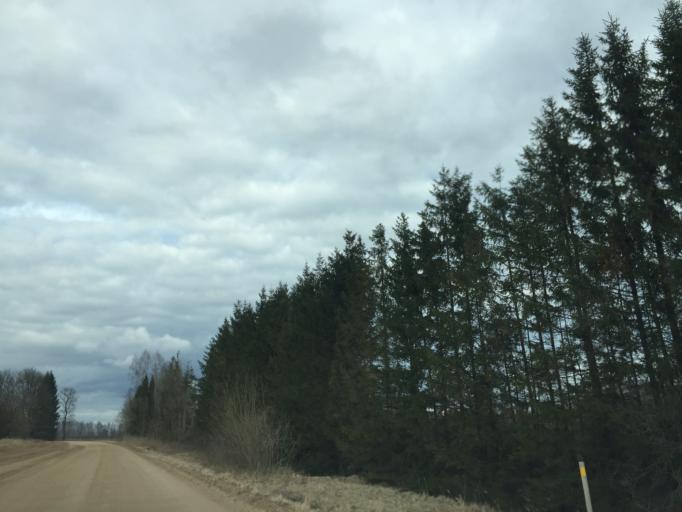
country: LV
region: Lielvarde
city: Lielvarde
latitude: 56.5191
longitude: 24.7543
